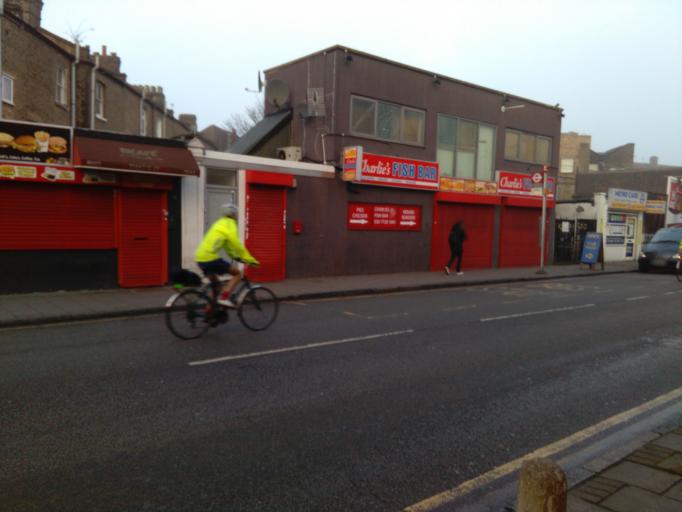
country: GB
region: England
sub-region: Greater London
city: Brixton Hill
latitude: 51.4644
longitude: -0.1294
